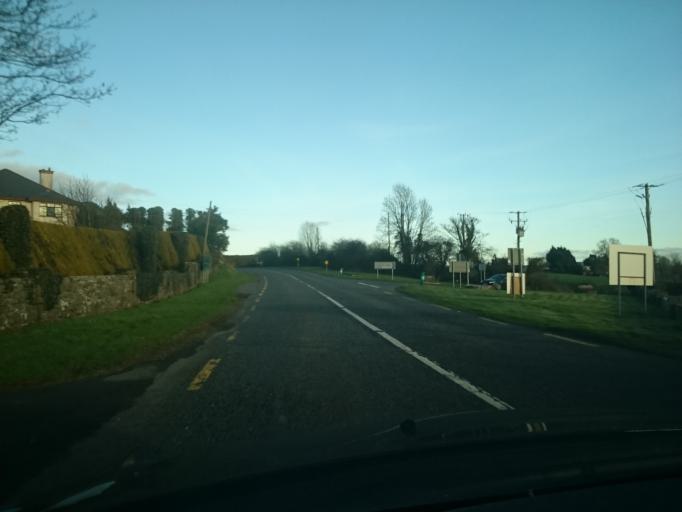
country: IE
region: Connaught
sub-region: Maigh Eo
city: Kiltamagh
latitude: 53.8014
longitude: -9.1255
